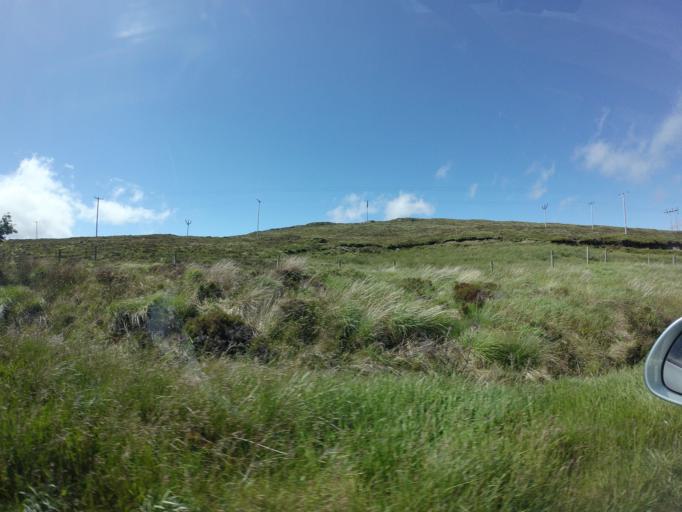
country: GB
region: Scotland
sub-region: Eilean Siar
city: Stornoway
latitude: 58.1284
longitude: -6.5065
